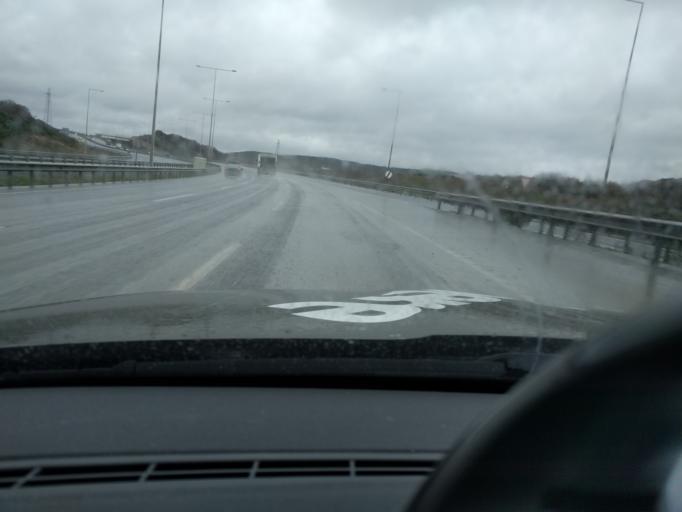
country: TR
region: Istanbul
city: Kemerburgaz
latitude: 41.2094
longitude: 28.8409
